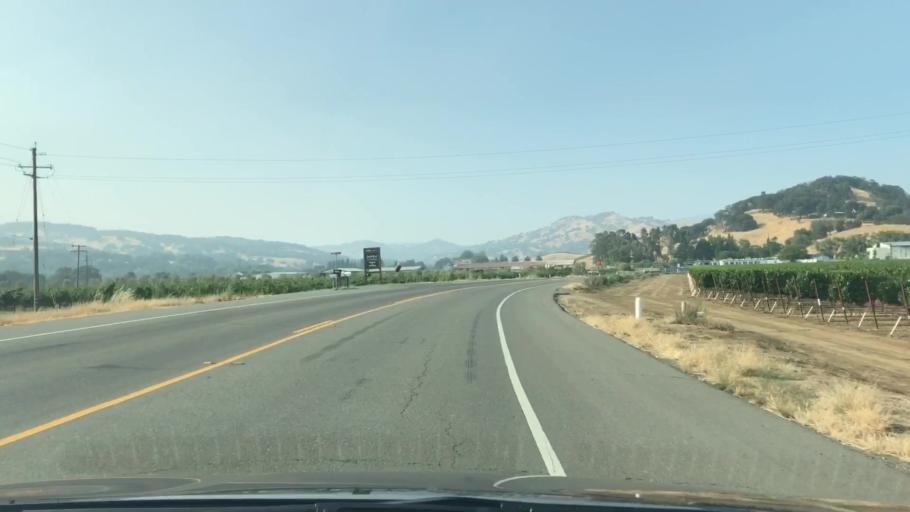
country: US
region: California
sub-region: Solano County
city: Green Valley
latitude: 38.2847
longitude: -122.1182
